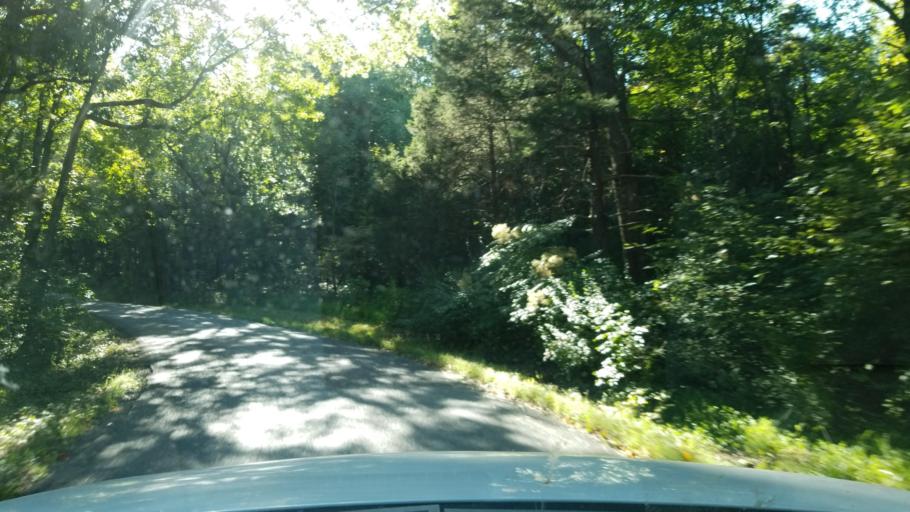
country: US
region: Illinois
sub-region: Hardin County
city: Elizabethtown
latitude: 37.6016
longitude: -88.3750
